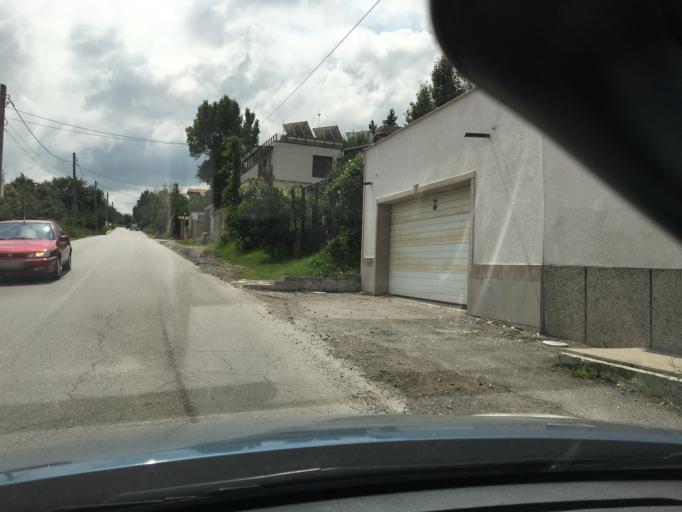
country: BG
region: Sofia-Capital
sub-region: Stolichna Obshtina
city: Sofia
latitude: 42.6059
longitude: 23.3662
